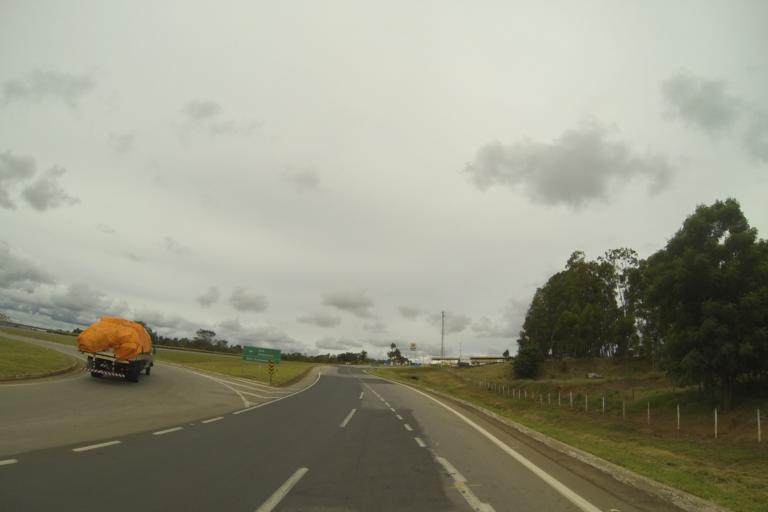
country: BR
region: Minas Gerais
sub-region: Ibia
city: Ibia
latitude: -19.5904
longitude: -46.4954
